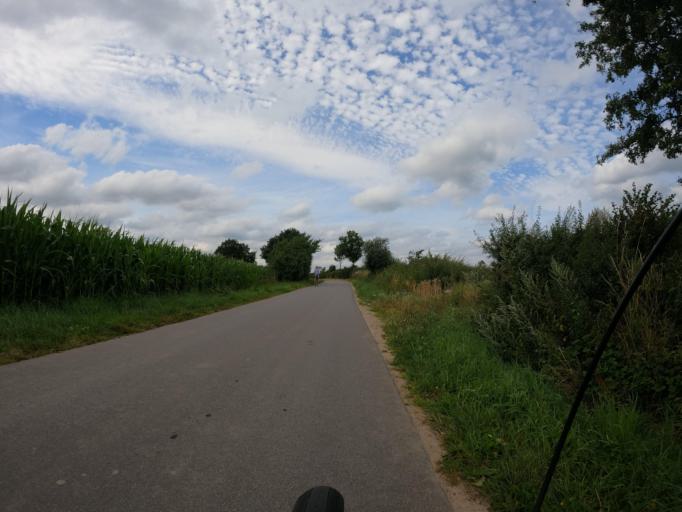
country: DE
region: Schleswig-Holstein
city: Steinberg
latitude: 54.7632
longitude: 9.7792
